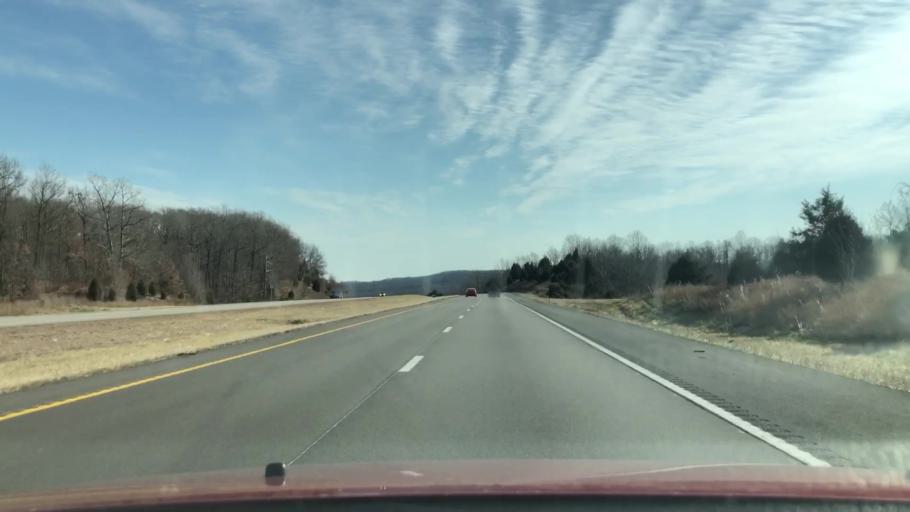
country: US
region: Missouri
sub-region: Wright County
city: Mansfield
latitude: 37.1144
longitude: -92.6731
